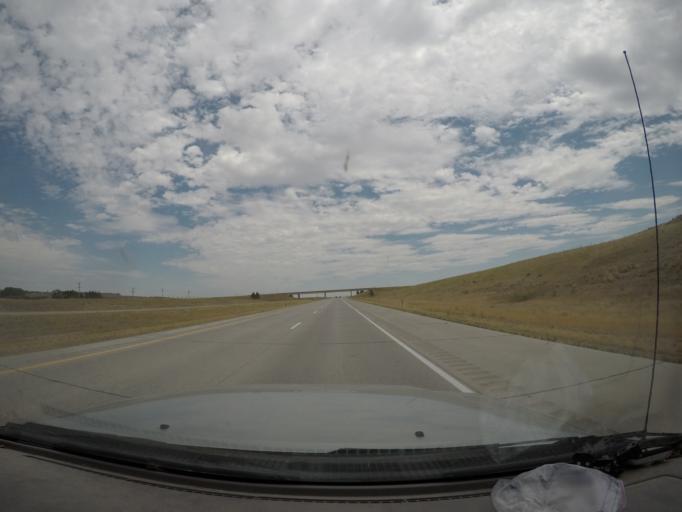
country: US
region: Nebraska
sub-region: Cheyenne County
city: Sidney
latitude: 41.2008
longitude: -103.2647
